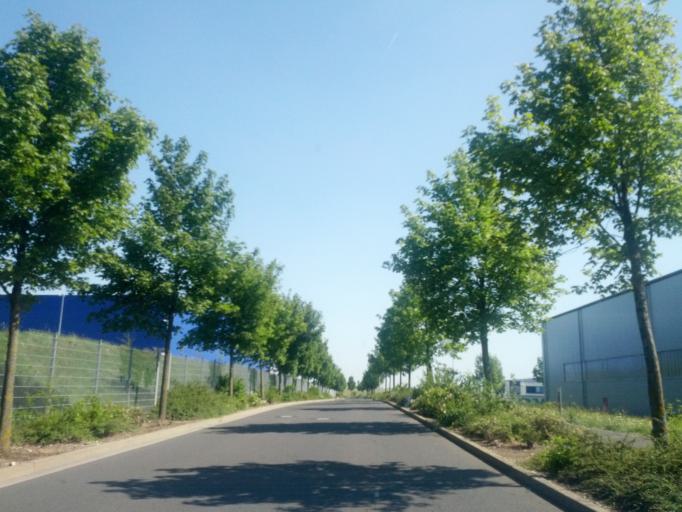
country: DE
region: Thuringia
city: Haina
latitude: 51.0001
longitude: 10.4484
